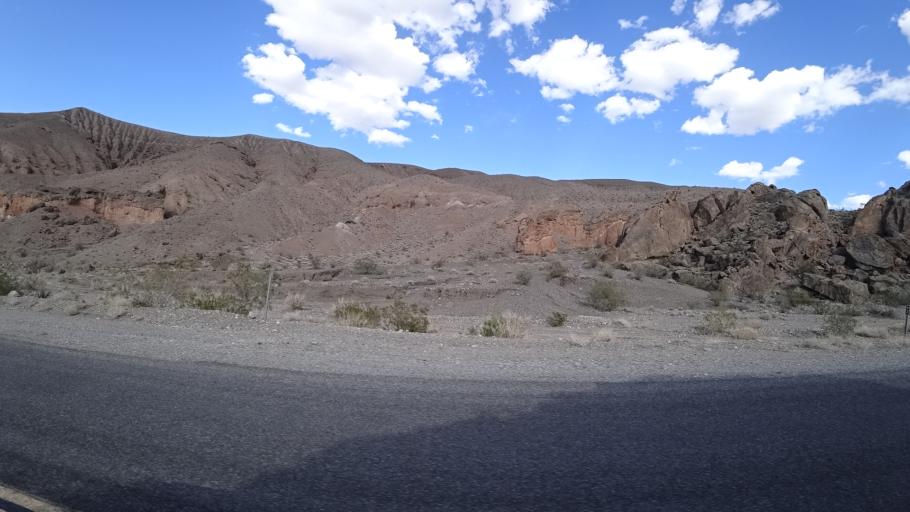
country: US
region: Nevada
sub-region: Nye County
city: Beatty
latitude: 36.4724
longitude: -117.2090
